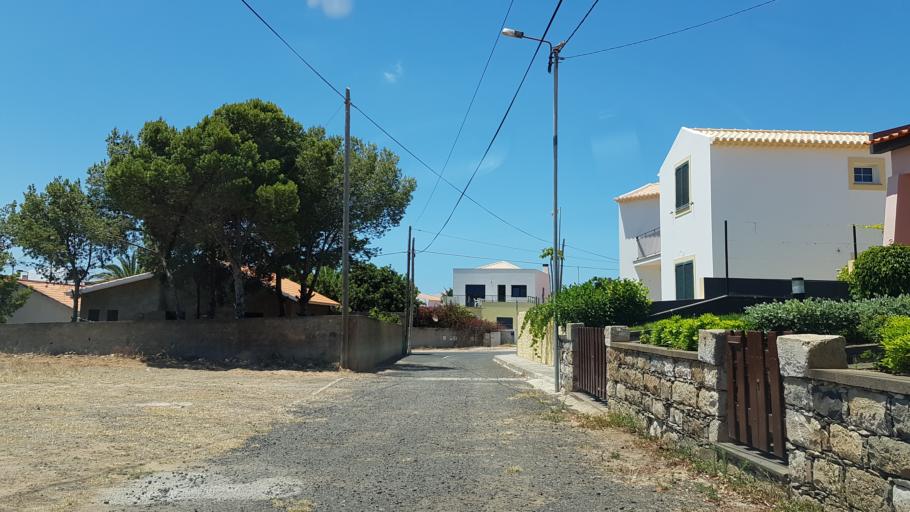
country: PT
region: Madeira
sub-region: Porto Santo
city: Vila de Porto Santo
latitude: 33.0524
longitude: -16.3511
